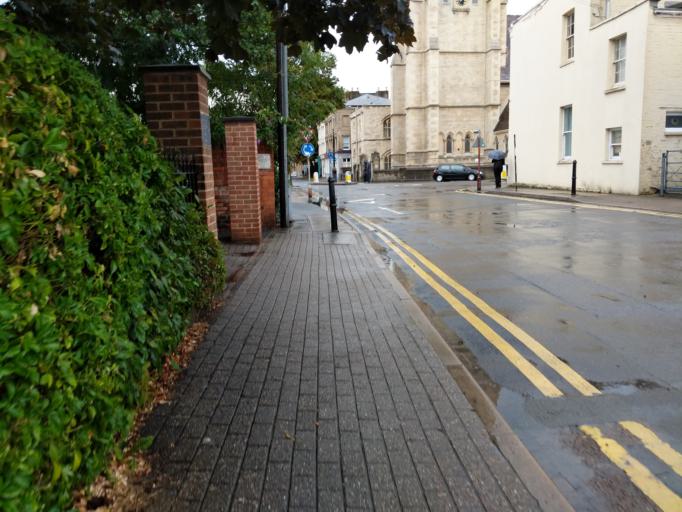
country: GB
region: England
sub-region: Gloucestershire
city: Cheltenham
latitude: 51.9021
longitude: -2.0809
